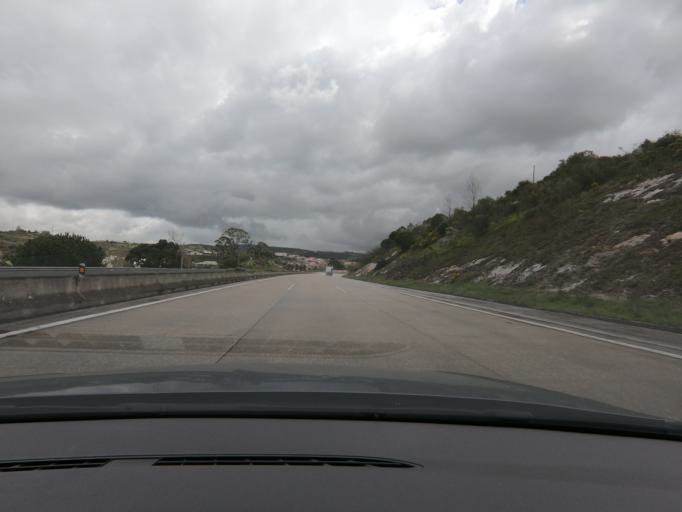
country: PT
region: Lisbon
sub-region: Loures
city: Bucelas
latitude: 38.8971
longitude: -9.1145
